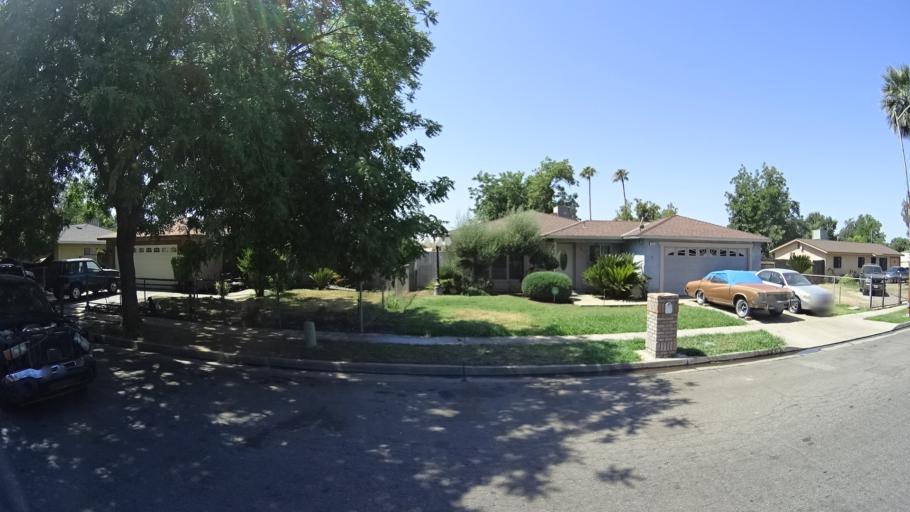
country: US
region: California
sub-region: Fresno County
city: Fresno
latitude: 36.7159
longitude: -119.8056
